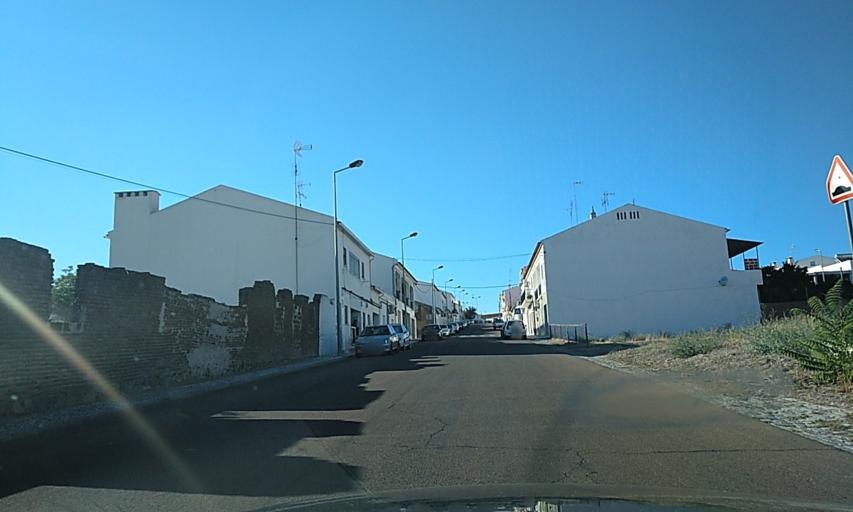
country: PT
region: Portalegre
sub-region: Campo Maior
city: Campo Maior
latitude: 39.0109
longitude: -7.0641
